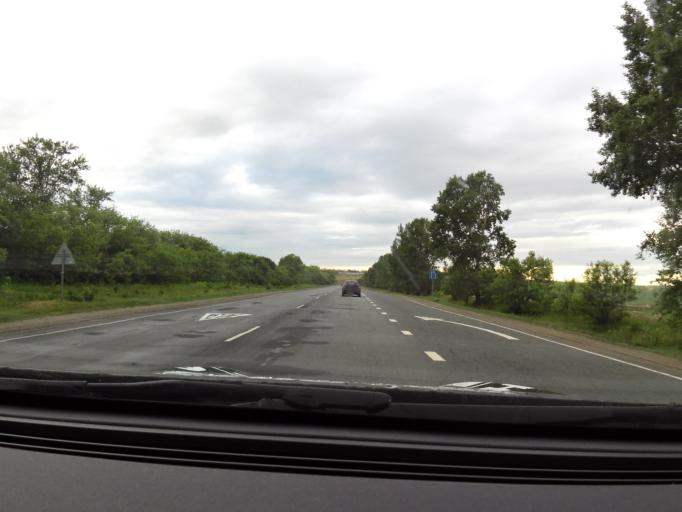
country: RU
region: Chuvashia
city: Yantikovo
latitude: 55.7899
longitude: 47.6915
